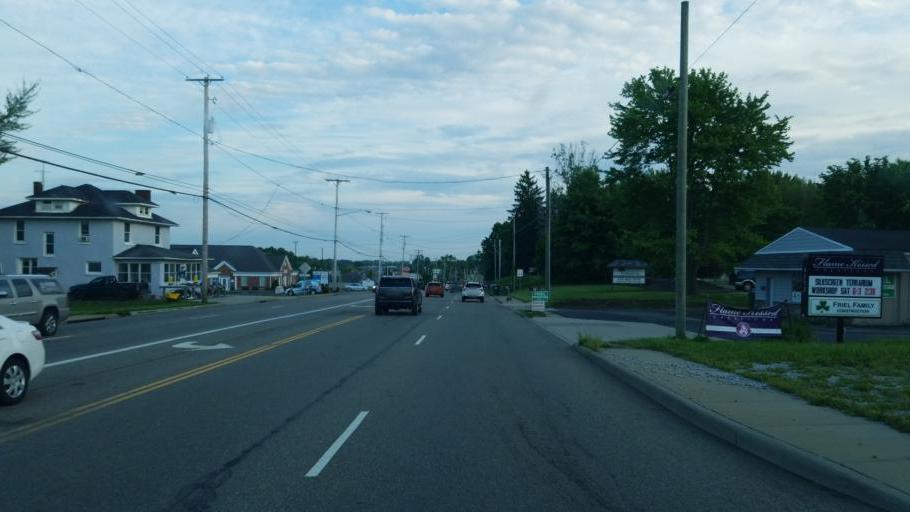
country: US
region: Ohio
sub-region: Stark County
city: Greentown
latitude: 40.9078
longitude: -81.4057
